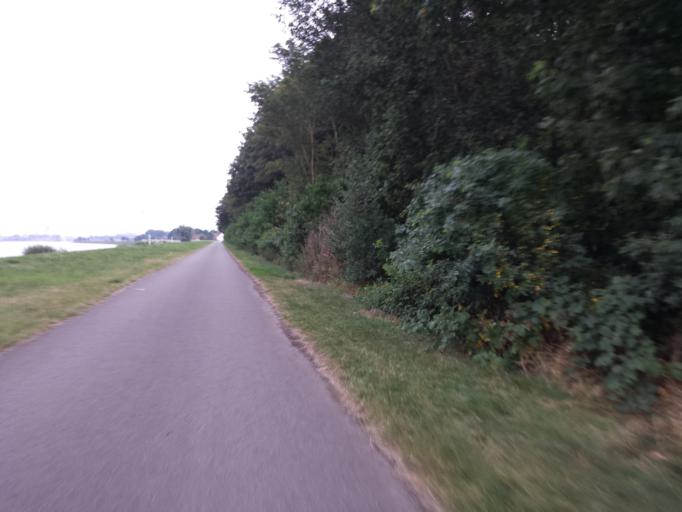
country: DE
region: Lower Saxony
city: Lemwerder
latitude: 53.1201
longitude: 8.6834
